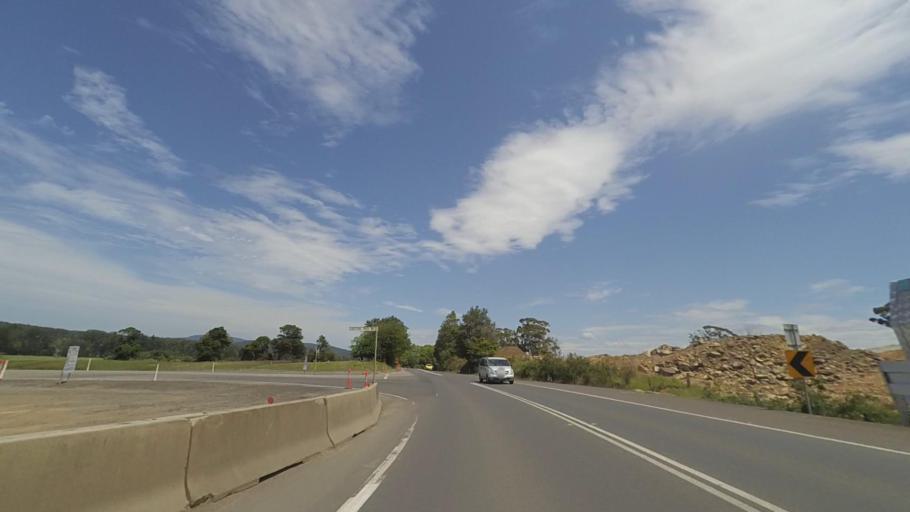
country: AU
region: New South Wales
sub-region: Shoalhaven Shire
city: Berry
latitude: -34.7595
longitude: 150.7406
